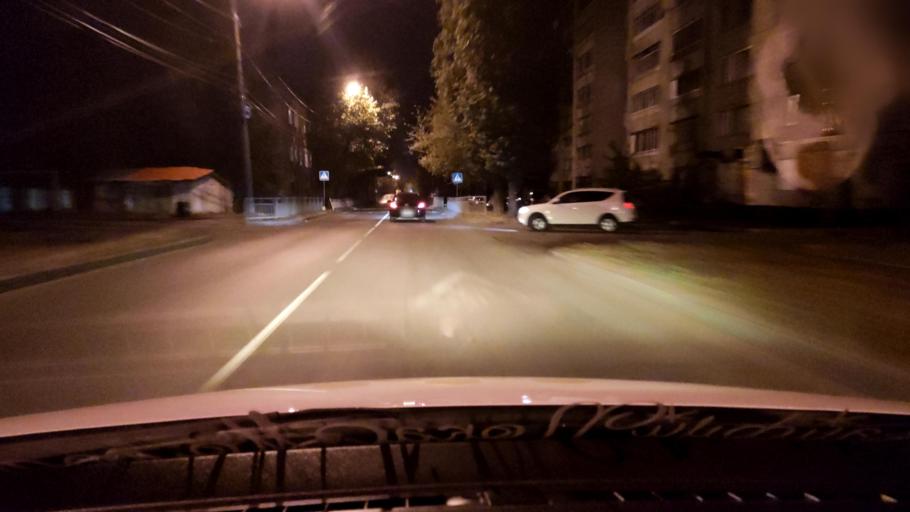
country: RU
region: Voronezj
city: Voronezh
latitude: 51.6468
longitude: 39.1713
